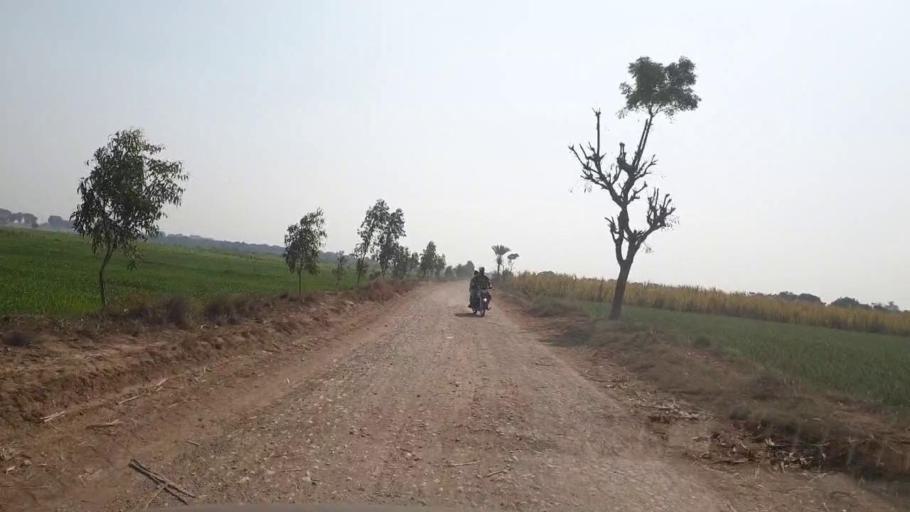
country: PK
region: Sindh
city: Bhit Shah
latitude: 25.7162
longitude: 68.5457
